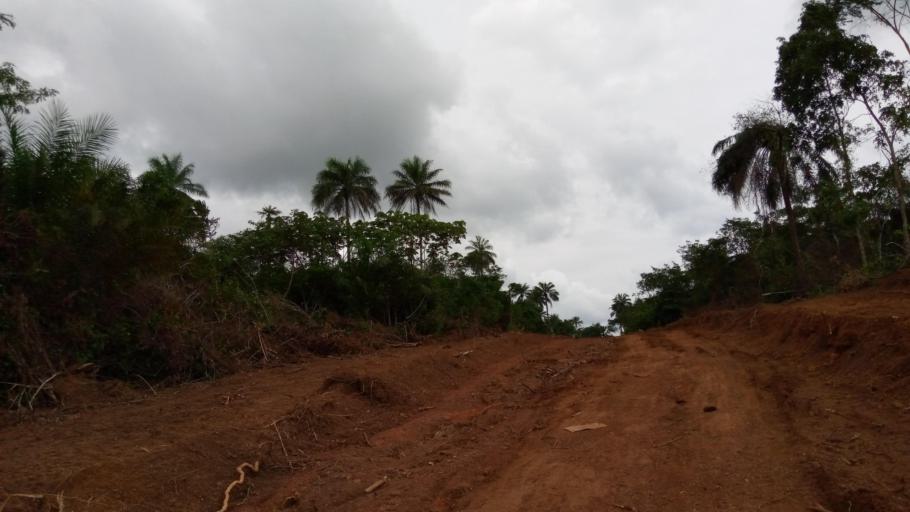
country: SL
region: Southern Province
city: Moyamba
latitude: 8.1950
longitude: -12.5393
